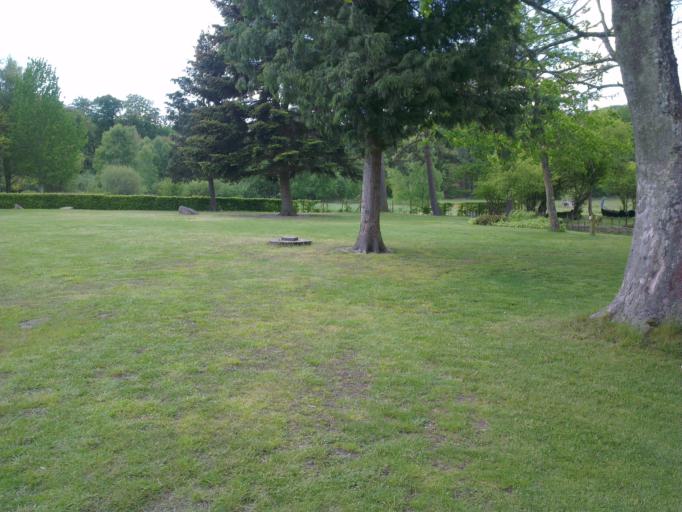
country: DK
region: Capital Region
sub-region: Frederikssund Kommune
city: Frederikssund
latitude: 55.8414
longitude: 12.0320
